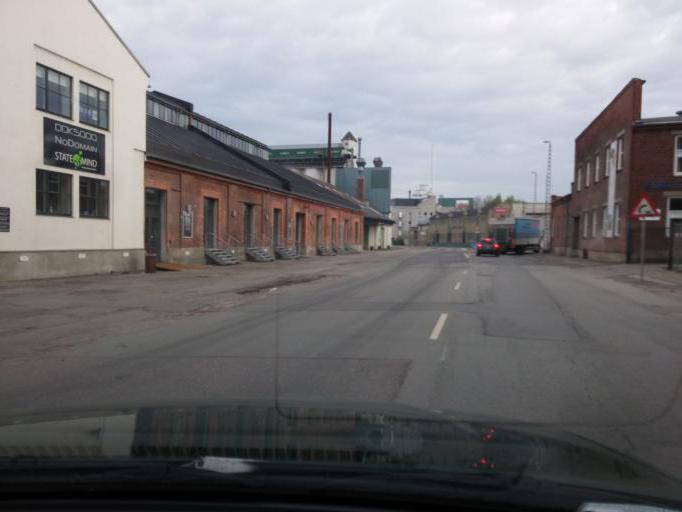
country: DK
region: South Denmark
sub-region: Odense Kommune
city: Odense
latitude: 55.4111
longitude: 10.3840
